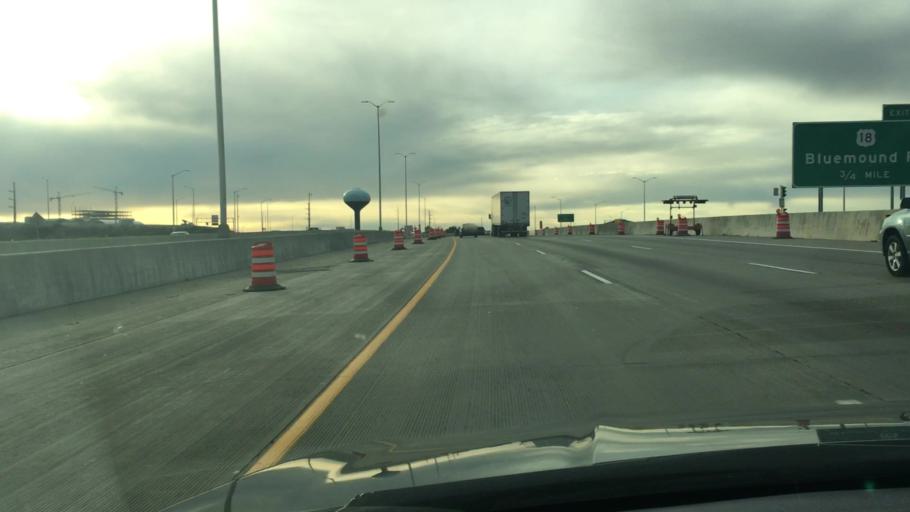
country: US
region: Wisconsin
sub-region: Milwaukee County
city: Wauwatosa
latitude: 43.0472
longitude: -88.0380
